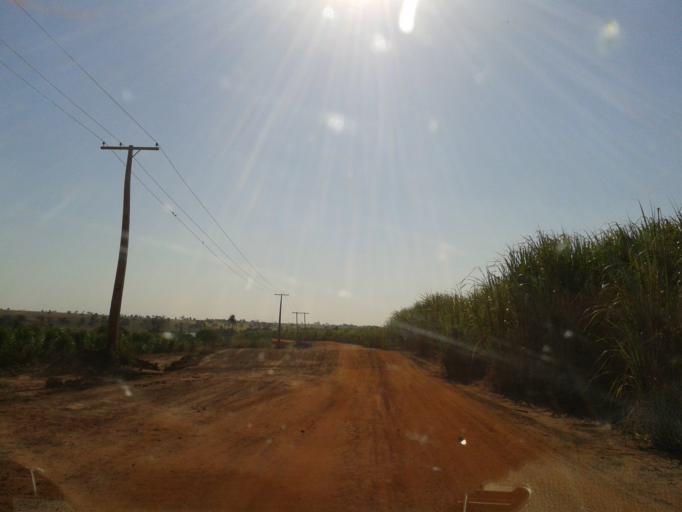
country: BR
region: Minas Gerais
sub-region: Santa Vitoria
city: Santa Vitoria
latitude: -18.7291
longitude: -50.2675
